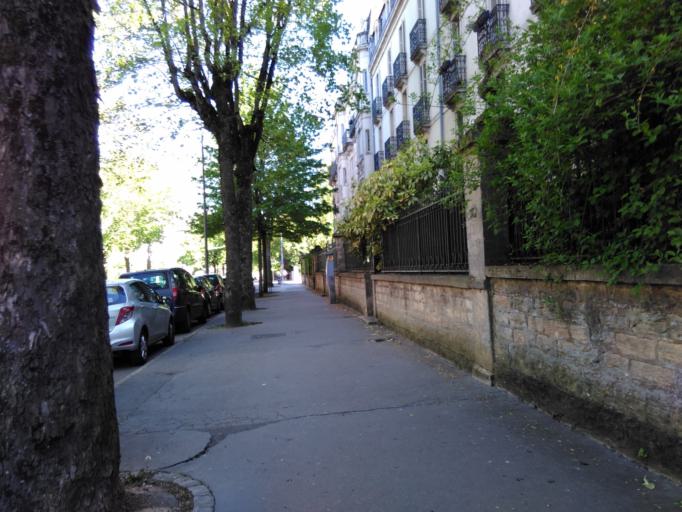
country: FR
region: Bourgogne
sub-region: Departement de la Cote-d'Or
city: Dijon
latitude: 47.3260
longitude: 5.0307
